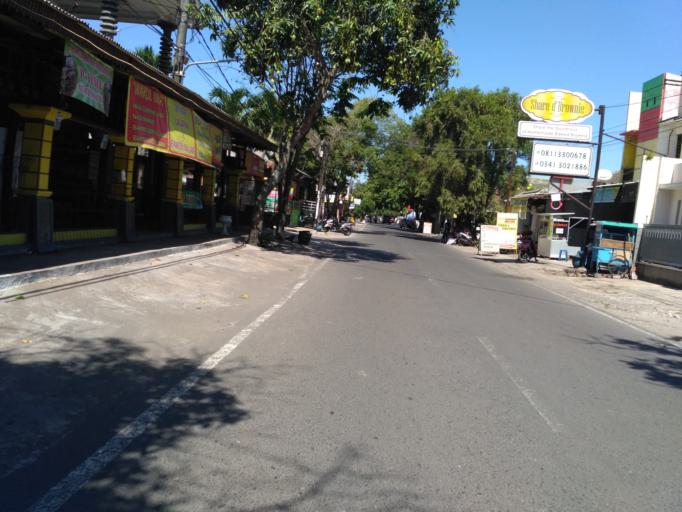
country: ID
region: East Java
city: Malang
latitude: -7.9753
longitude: 112.6655
